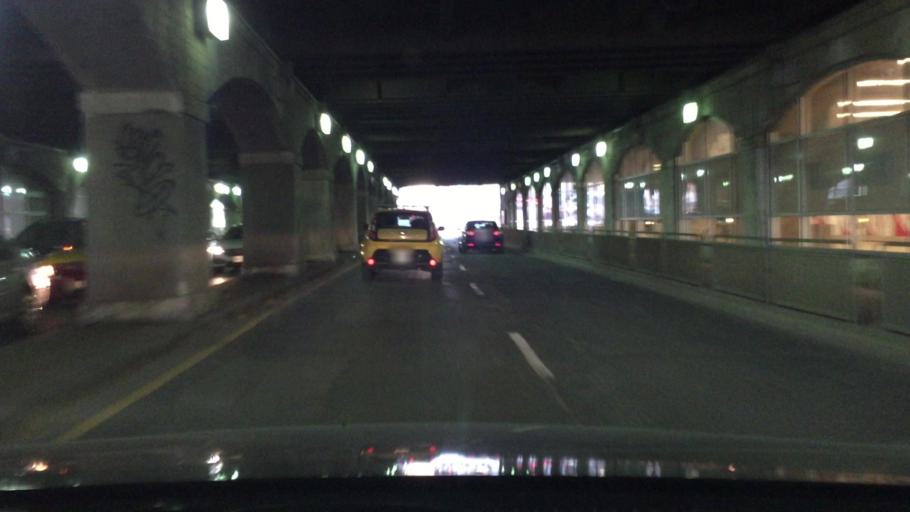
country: CA
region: Ontario
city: Toronto
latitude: 43.6437
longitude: -79.3817
